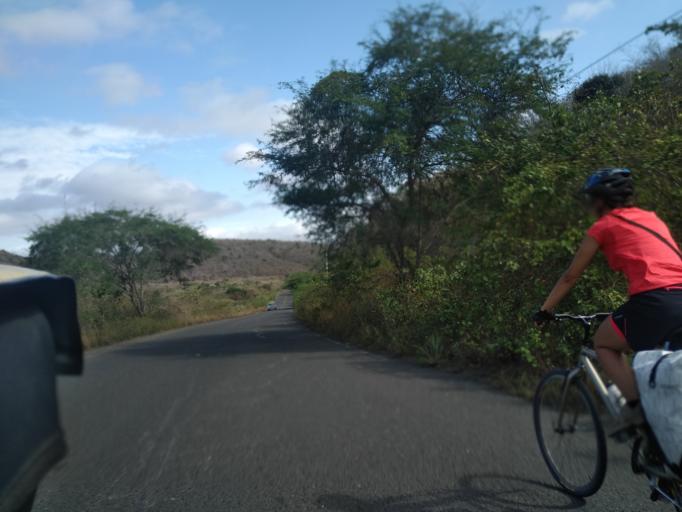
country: EC
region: Manabi
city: Jipijapa
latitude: -1.4528
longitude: -80.7595
